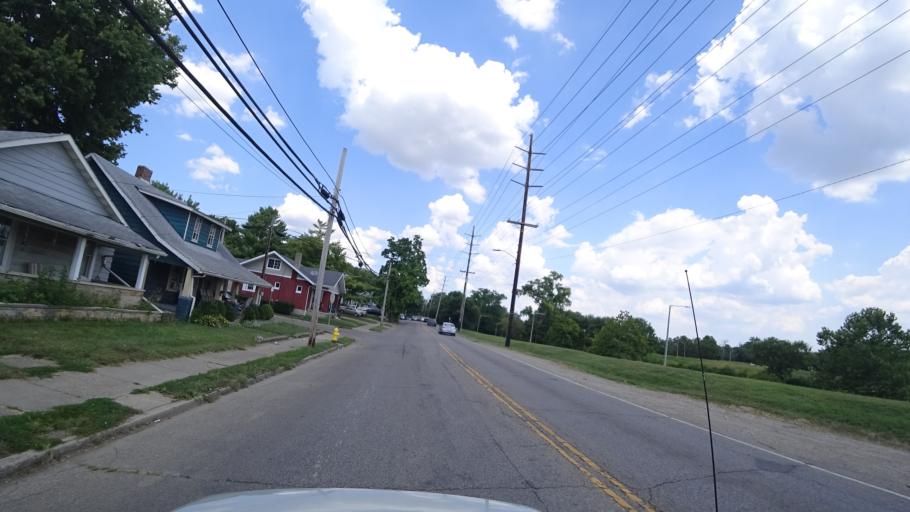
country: US
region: Ohio
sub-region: Butler County
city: Hamilton
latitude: 39.4143
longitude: -84.5569
